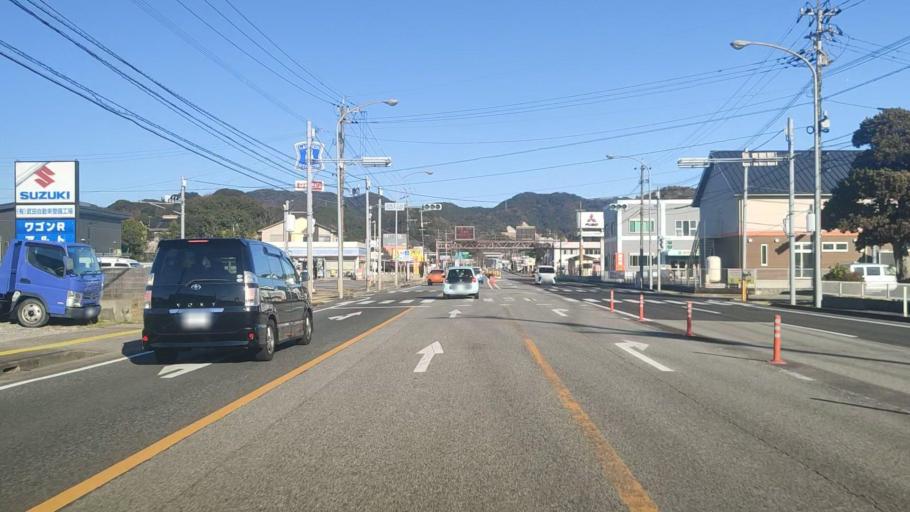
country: JP
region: Miyazaki
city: Nobeoka
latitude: 32.4910
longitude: 131.6638
